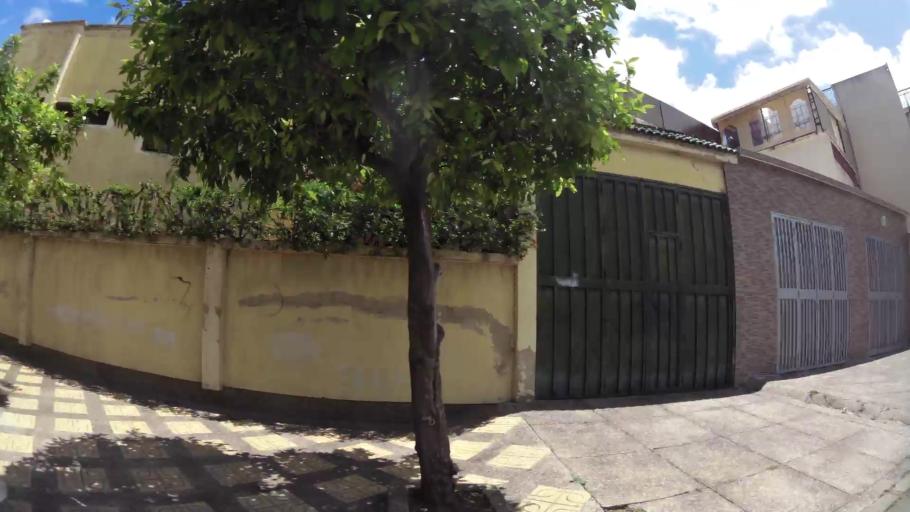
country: MA
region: Fes-Boulemane
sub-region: Fes
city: Fes
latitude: 34.0370
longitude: -5.0225
